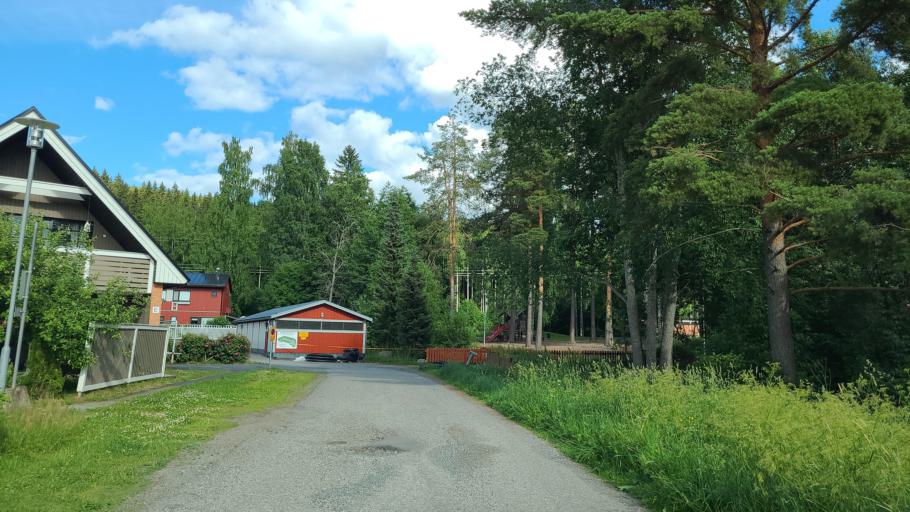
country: FI
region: Northern Savo
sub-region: Kuopio
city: Kuopio
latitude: 62.9259
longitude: 27.6340
